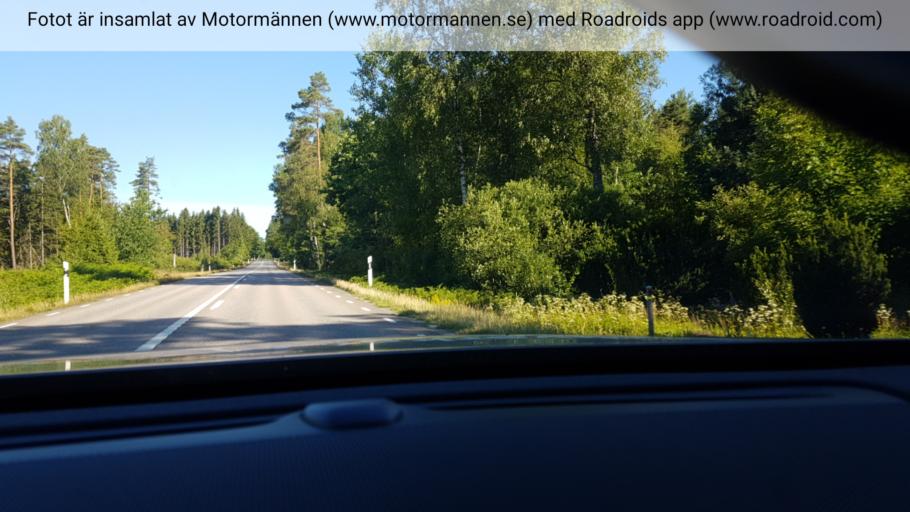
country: SE
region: Kronoberg
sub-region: Markaryds Kommun
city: Markaryd
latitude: 56.4117
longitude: 13.6373
